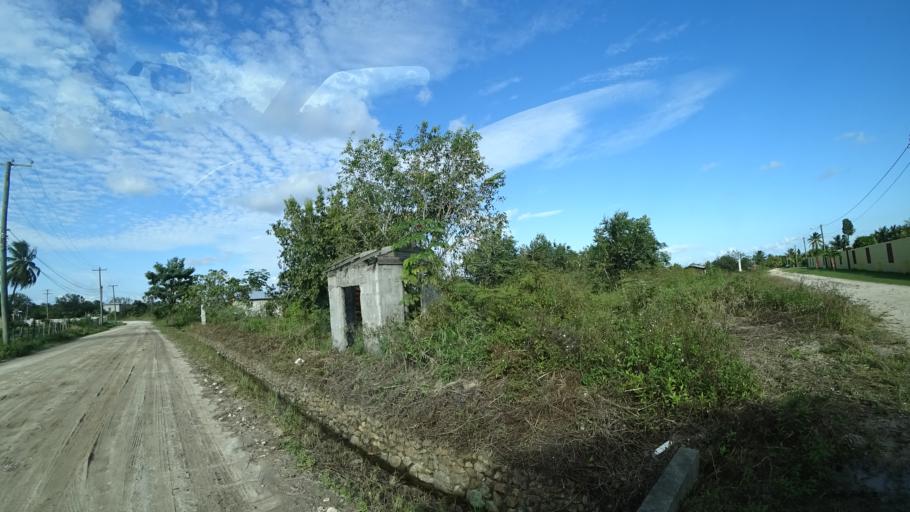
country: BZ
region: Belize
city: Belize City
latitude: 17.5552
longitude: -88.4017
